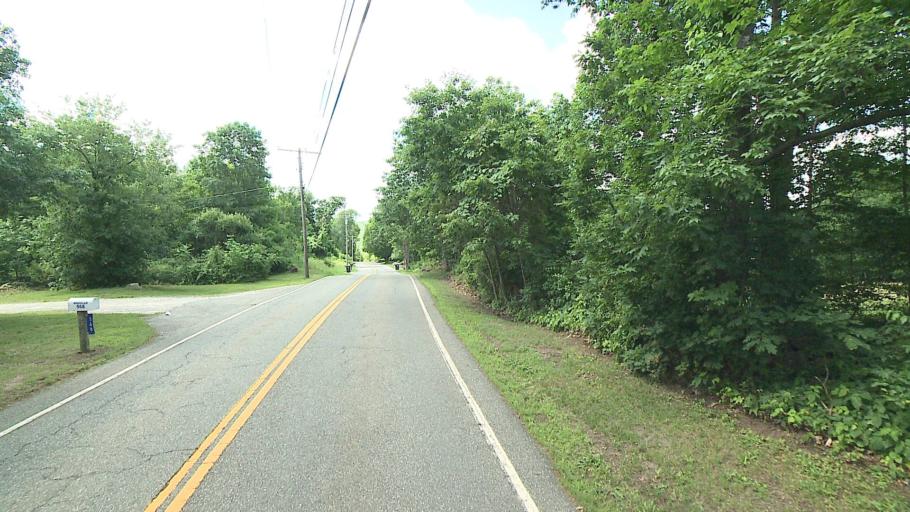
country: US
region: Connecticut
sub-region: Litchfield County
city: West Torrington
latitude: 41.8350
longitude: -73.1585
